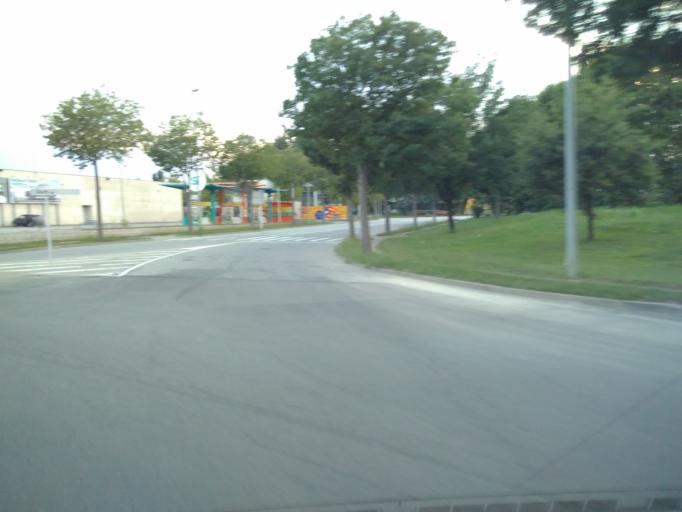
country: ES
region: Catalonia
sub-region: Provincia de Barcelona
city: Vic
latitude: 41.9459
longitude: 2.2526
